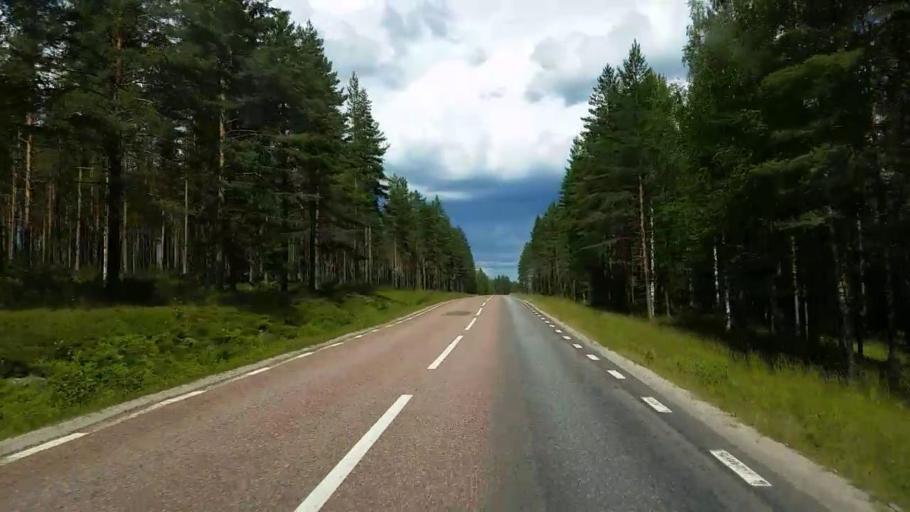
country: SE
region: Gaevleborg
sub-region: Ovanakers Kommun
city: Edsbyn
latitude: 61.3123
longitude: 15.5068
